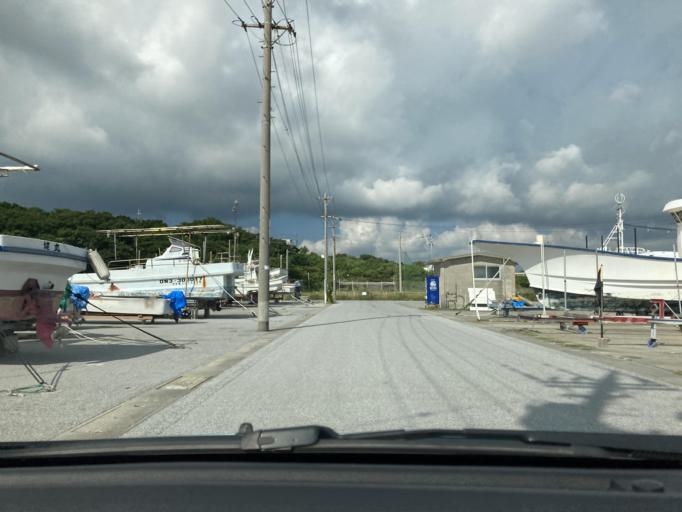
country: JP
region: Okinawa
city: Itoman
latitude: 26.1303
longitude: 127.7760
